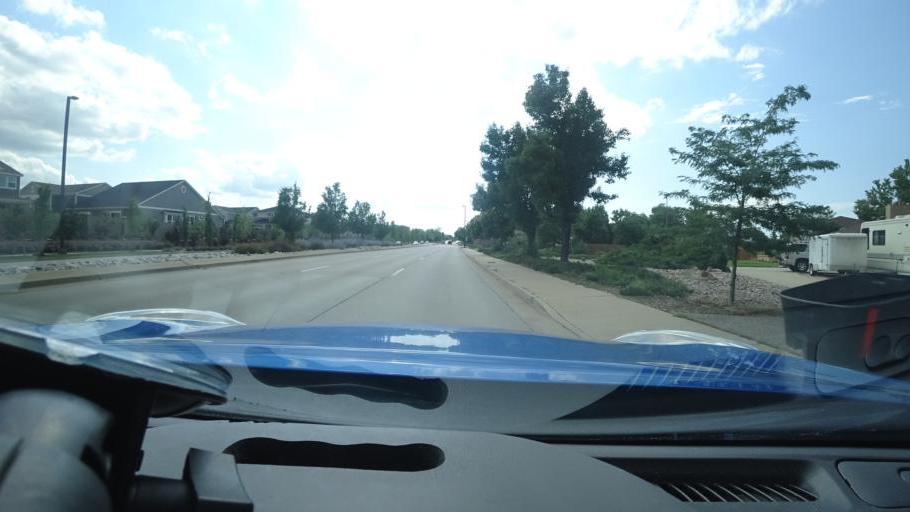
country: US
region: Colorado
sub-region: Adams County
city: Aurora
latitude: 39.6966
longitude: -104.8711
